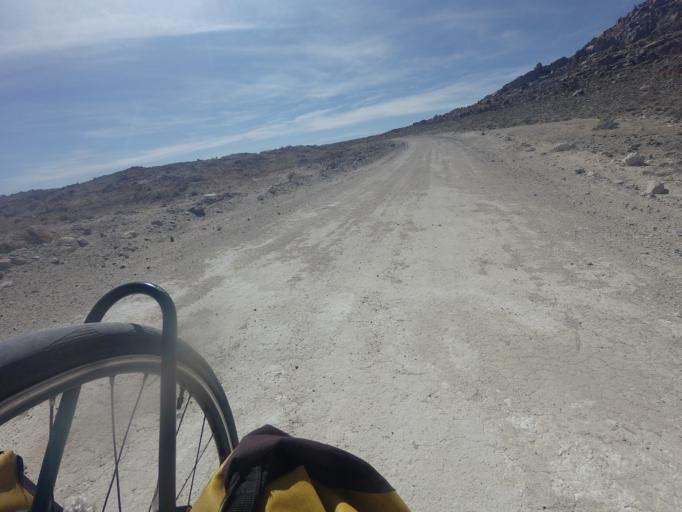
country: US
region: California
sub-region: San Bernardino County
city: Searles Valley
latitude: 35.6041
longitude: -117.3809
